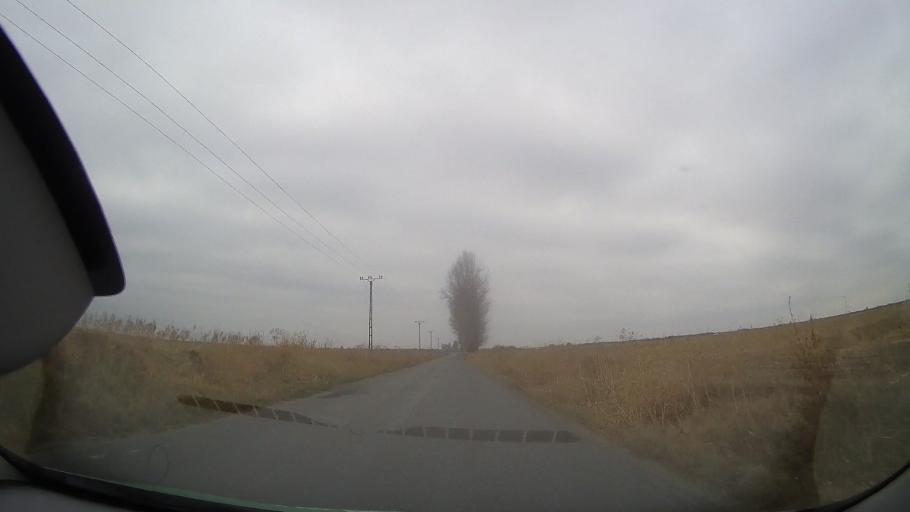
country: RO
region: Buzau
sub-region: Comuna Pogoanele
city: Pogoanele
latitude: 44.9435
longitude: 27.0080
